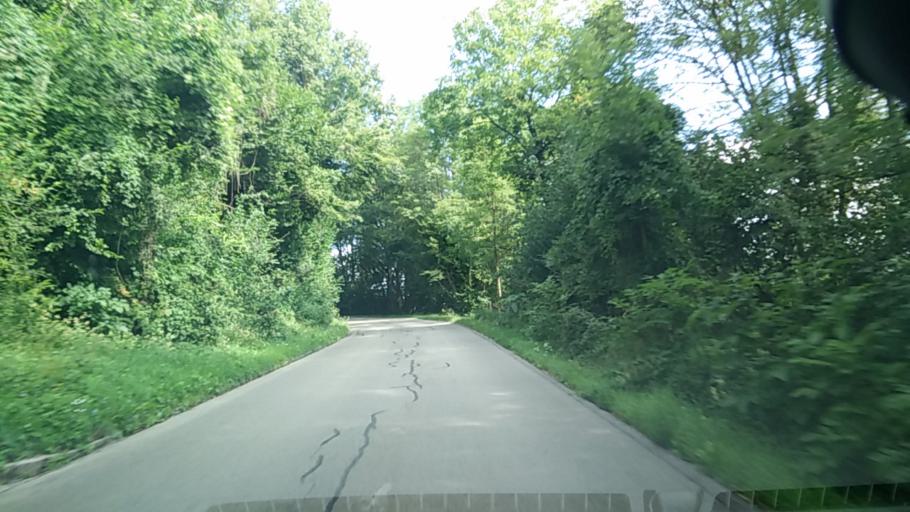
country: AT
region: Carinthia
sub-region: Politischer Bezirk Volkermarkt
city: Voelkermarkt
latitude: 46.6790
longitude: 14.5704
